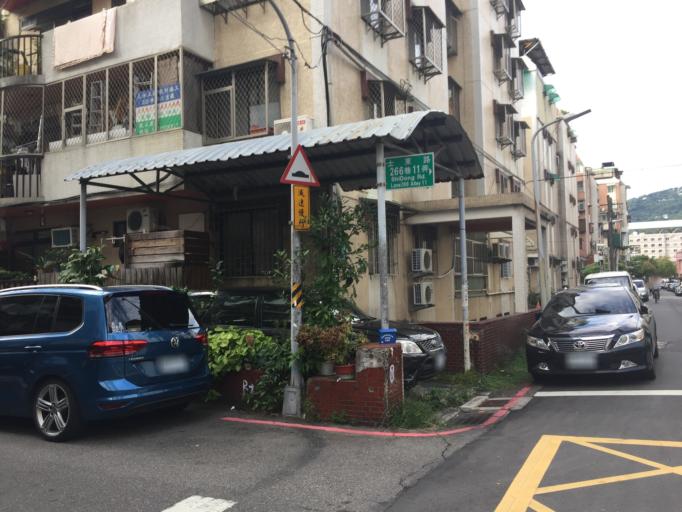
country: TW
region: Taipei
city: Taipei
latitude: 25.1118
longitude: 121.5367
